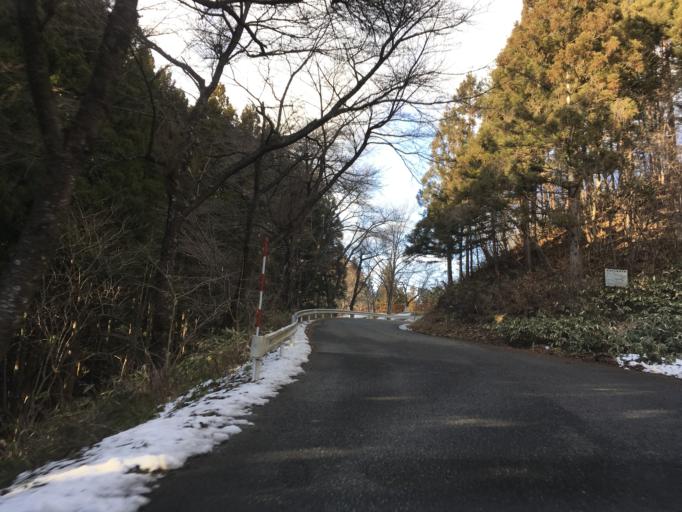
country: JP
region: Miyagi
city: Furukawa
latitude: 38.8210
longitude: 140.8320
